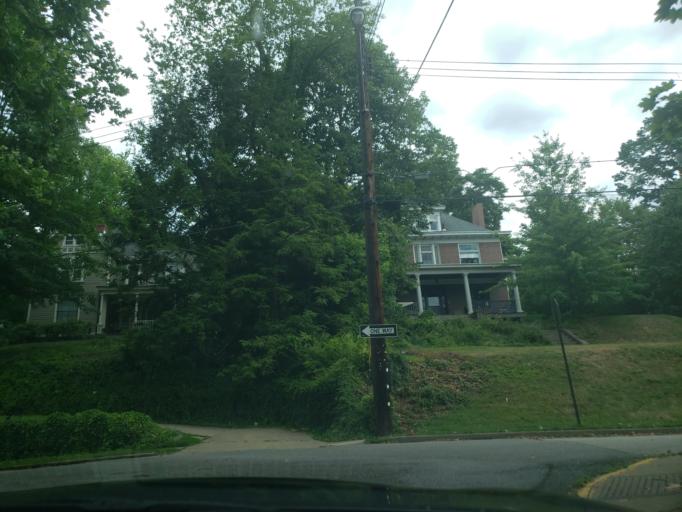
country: US
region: Pennsylvania
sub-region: Allegheny County
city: Ben Avon
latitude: 40.5096
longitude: -80.0828
